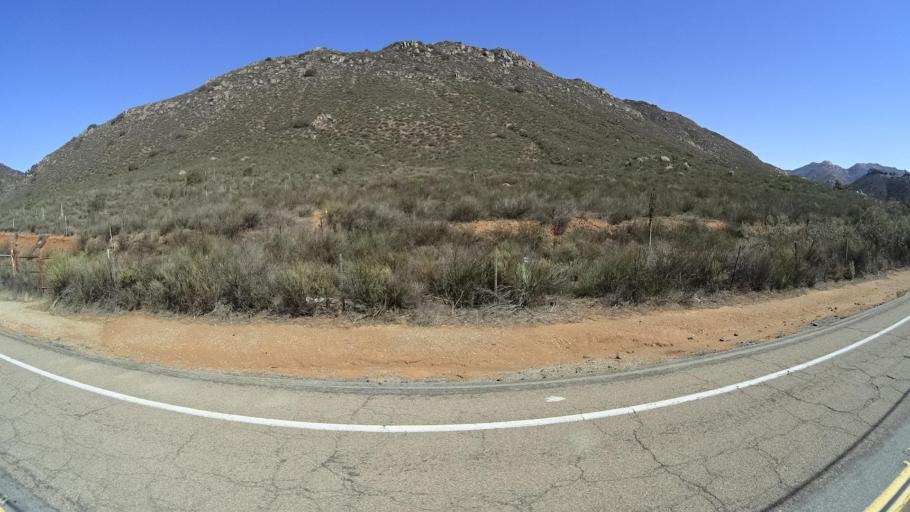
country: US
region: California
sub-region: San Diego County
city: Alpine
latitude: 32.7960
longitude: -116.7460
